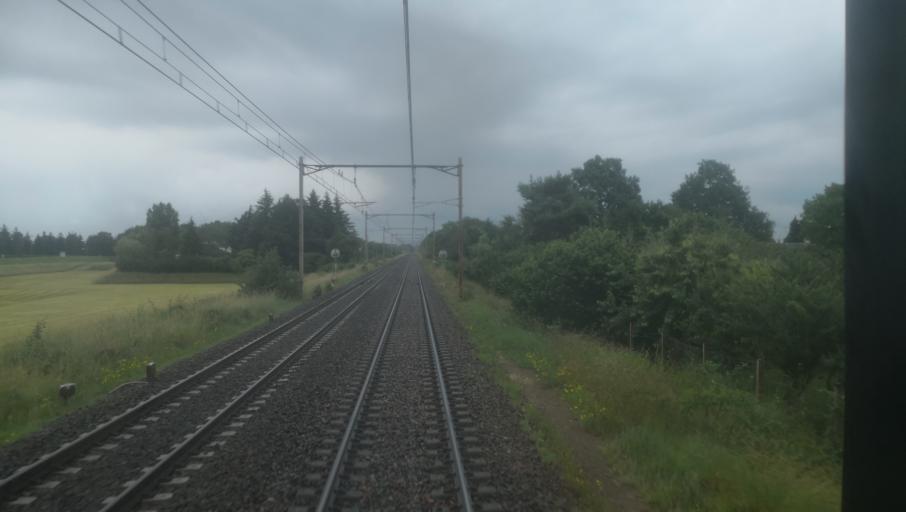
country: FR
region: Centre
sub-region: Departement du Loiret
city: Saint-Jean-le-Blanc
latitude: 47.8804
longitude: 1.9277
